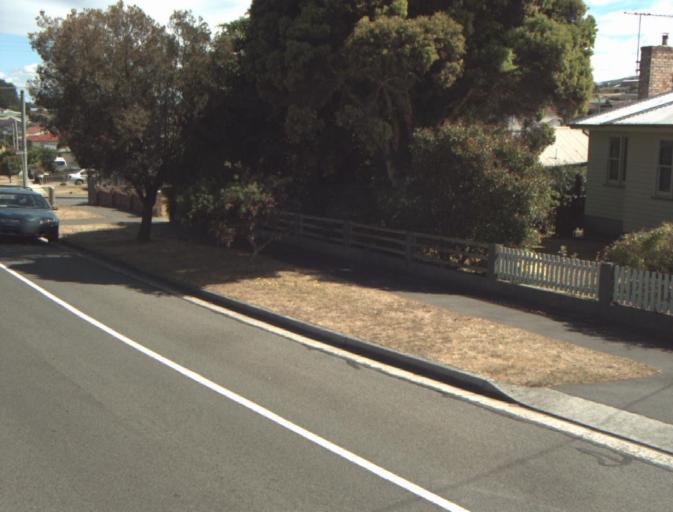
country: AU
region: Tasmania
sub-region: Launceston
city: Mayfield
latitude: -41.3859
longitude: 147.1136
